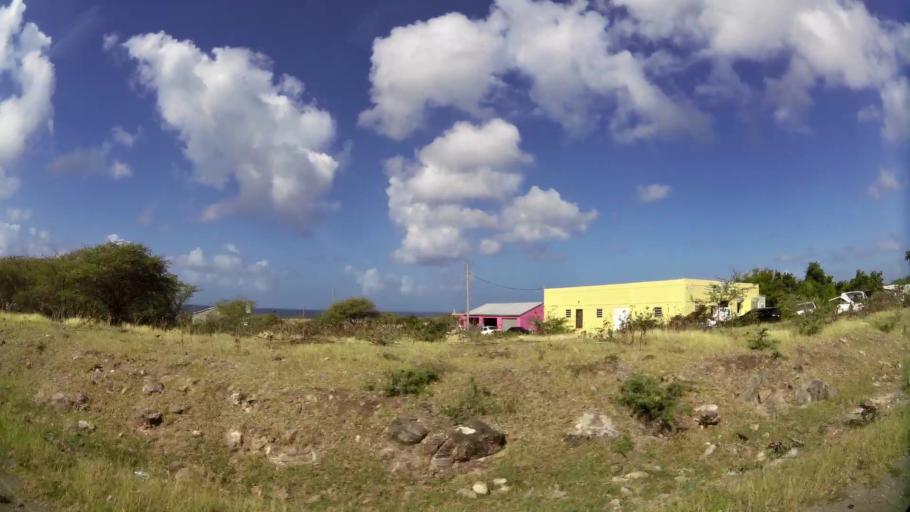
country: KN
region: Saint Paul Charlestown
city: Charlestown
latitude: 17.1163
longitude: -62.6199
